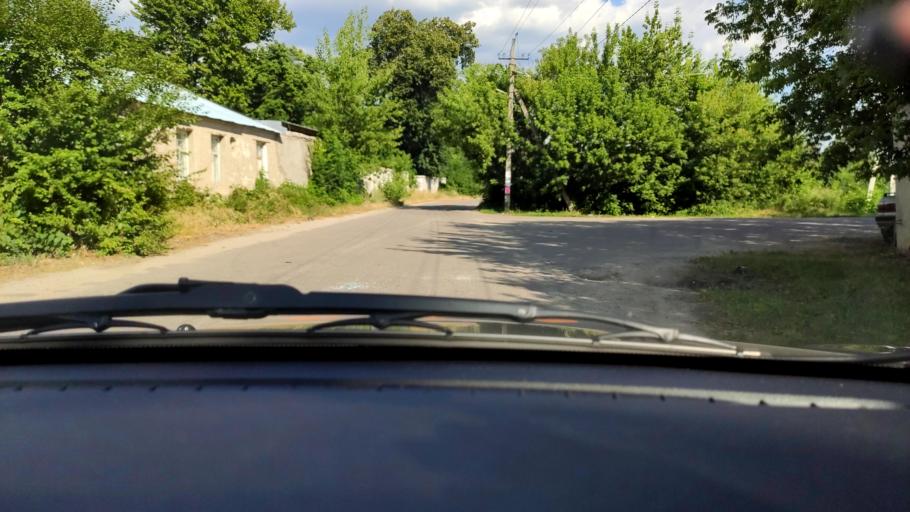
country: RU
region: Voronezj
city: Ramon'
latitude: 51.8250
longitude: 39.2703
